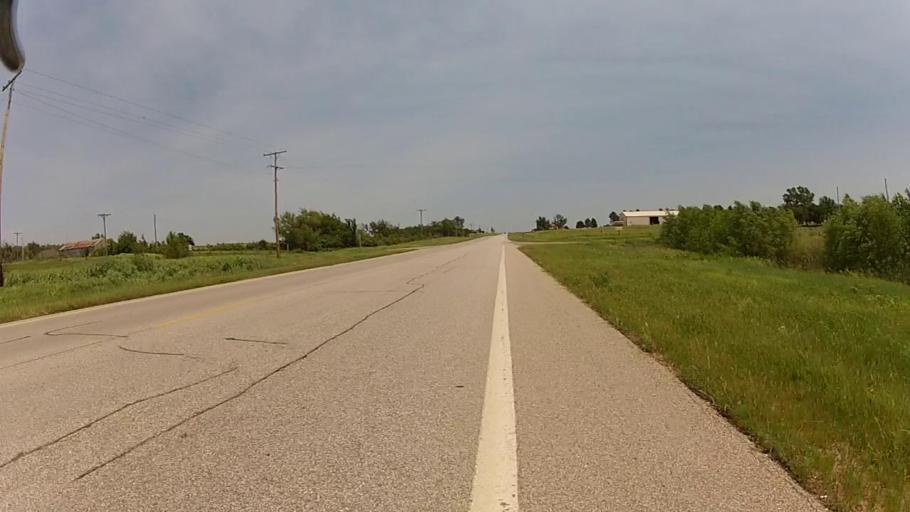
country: US
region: Kansas
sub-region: Cowley County
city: Arkansas City
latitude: 37.0565
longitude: -97.1127
